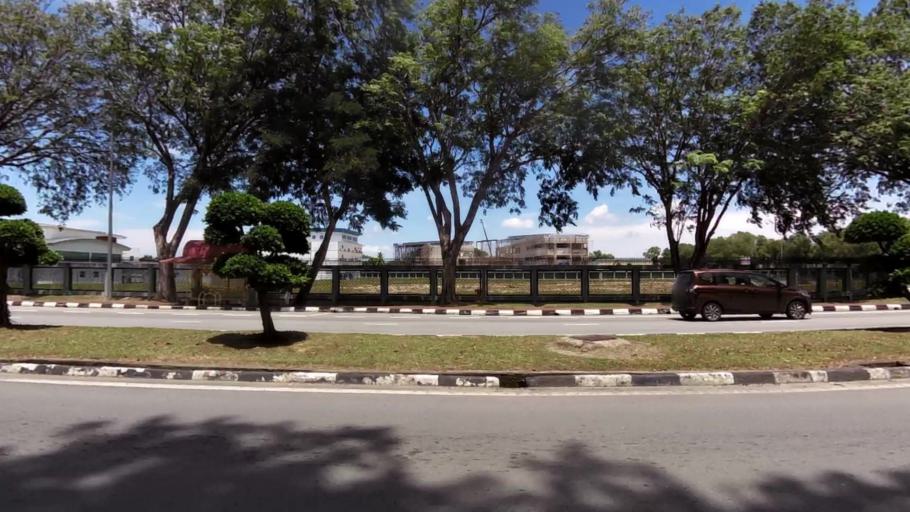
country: BN
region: Brunei and Muara
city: Bandar Seri Begawan
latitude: 4.9342
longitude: 114.9413
